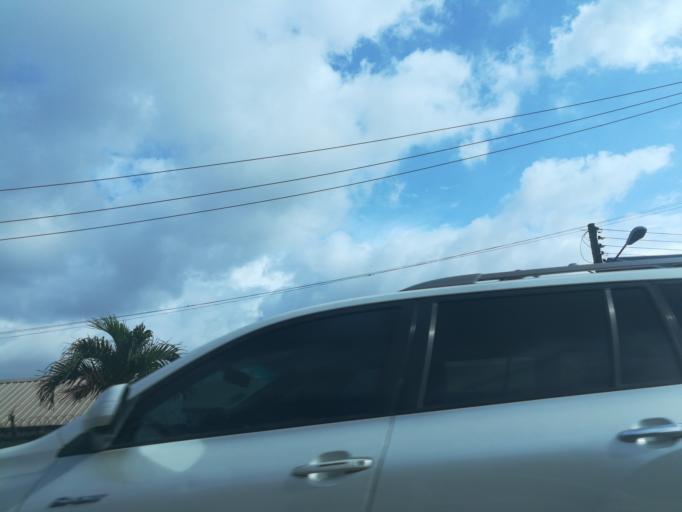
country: NG
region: Lagos
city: Ikeja
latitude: 6.6186
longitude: 3.3633
